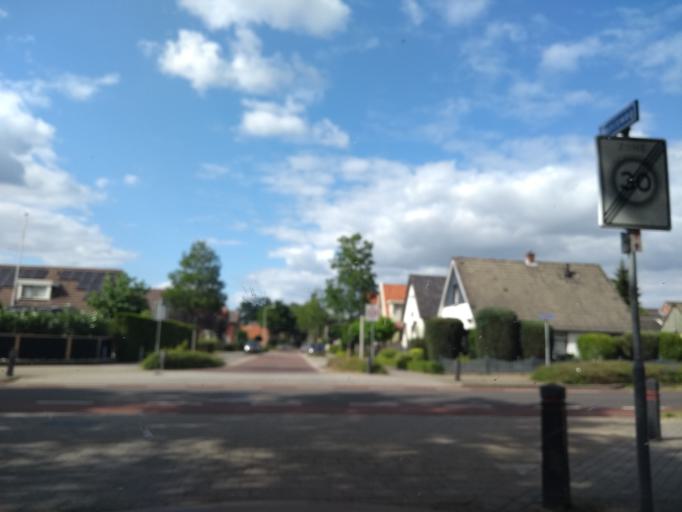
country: NL
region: Overijssel
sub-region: Gemeente Hof van Twente
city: Markelo
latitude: 52.3016
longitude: 6.5035
